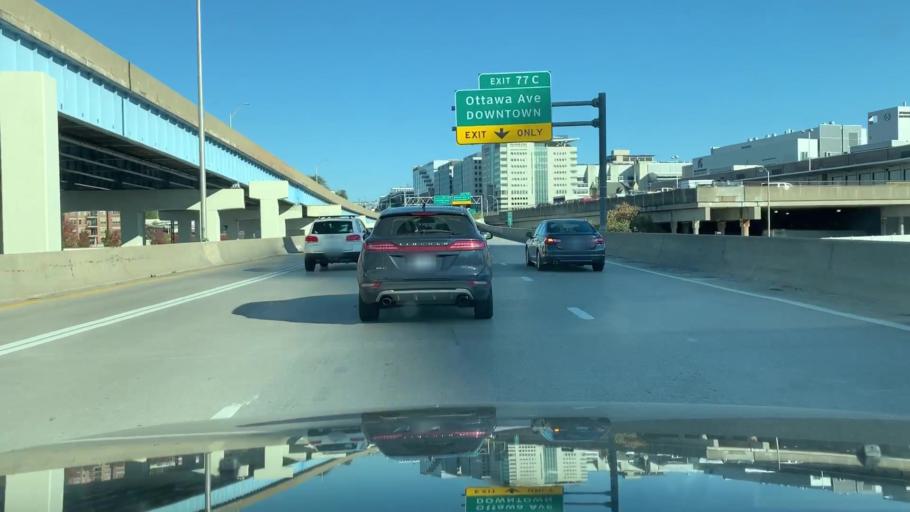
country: US
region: Michigan
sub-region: Kent County
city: Grand Rapids
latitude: 42.9724
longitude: -85.6746
